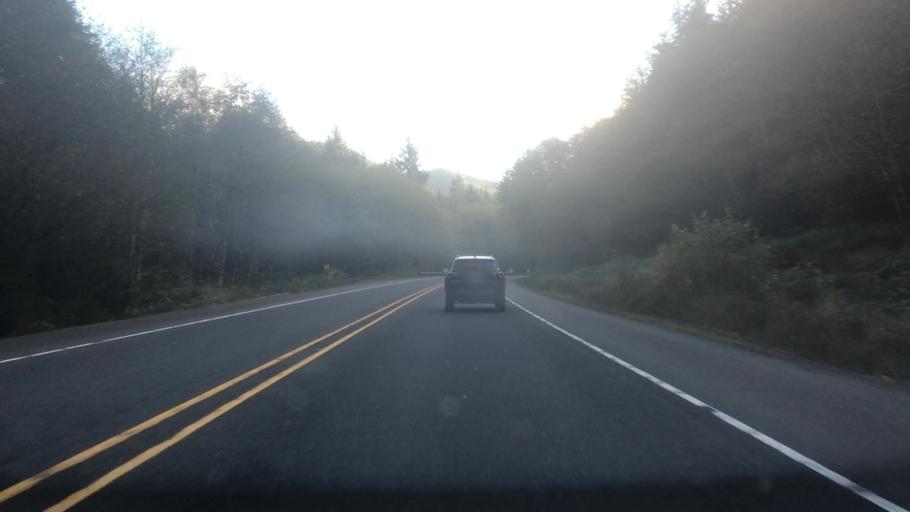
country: US
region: Oregon
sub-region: Clatsop County
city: Cannon Beach
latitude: 45.9314
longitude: -123.9277
